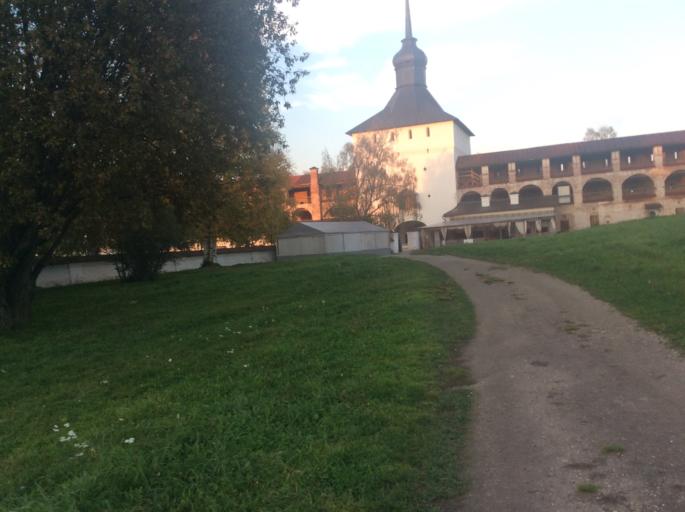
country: RU
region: Vologda
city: Kirillov
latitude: 59.8578
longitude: 38.3696
